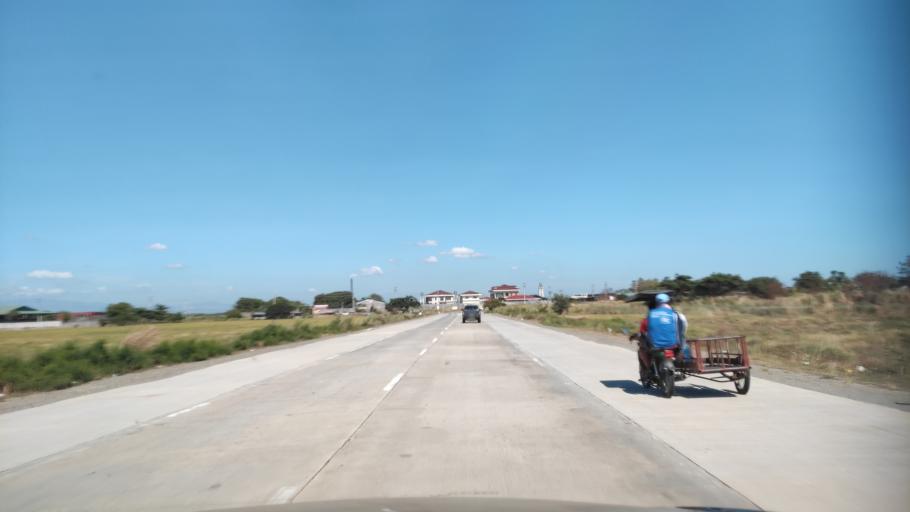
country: PH
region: Central Luzon
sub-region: Province of Tarlac
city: Salcedo
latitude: 15.8702
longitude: 120.6063
